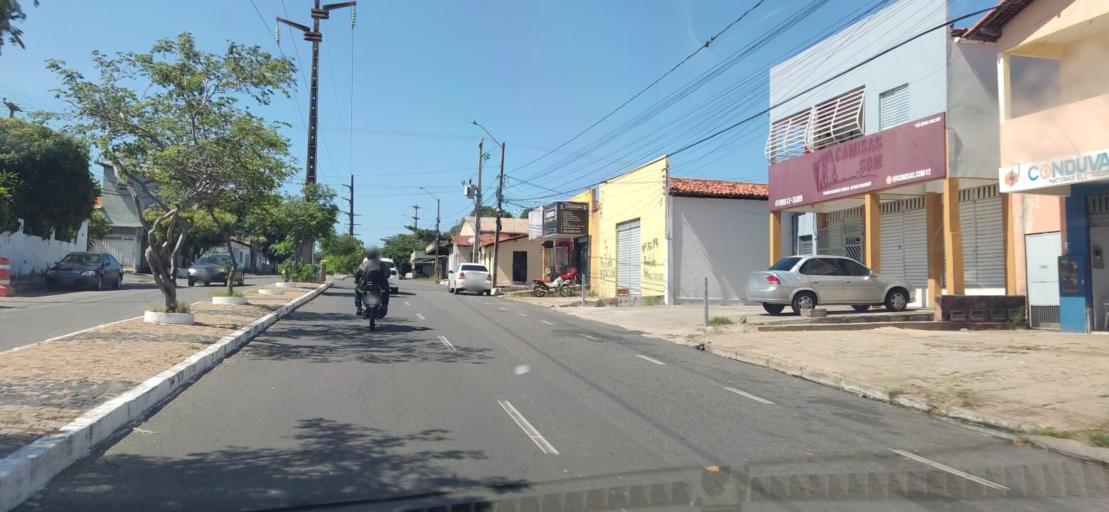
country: BR
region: Piaui
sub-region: Teresina
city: Teresina
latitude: -5.1208
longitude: -42.8092
